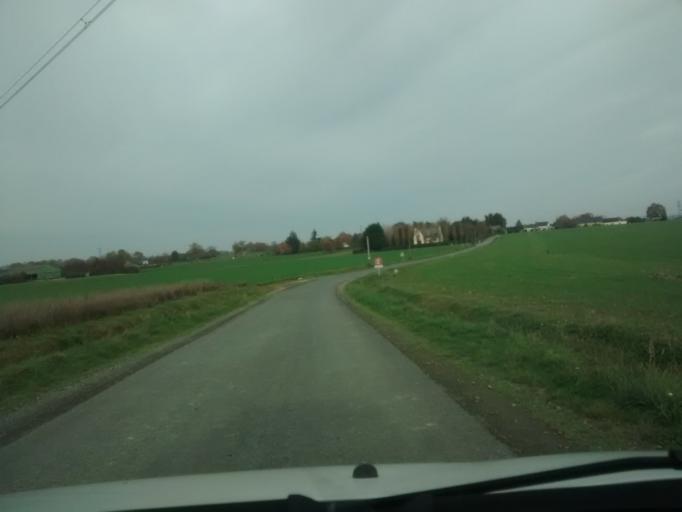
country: FR
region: Brittany
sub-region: Departement d'Ille-et-Vilaine
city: Noyal-sur-Vilaine
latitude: 48.0906
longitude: -1.5295
